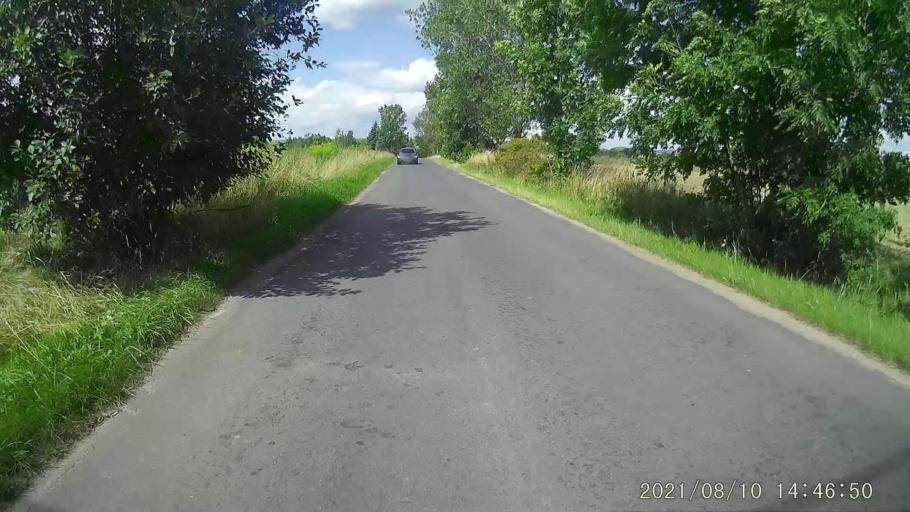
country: PL
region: Lower Silesian Voivodeship
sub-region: Powiat klodzki
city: Radkow
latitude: 50.5268
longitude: 16.4127
